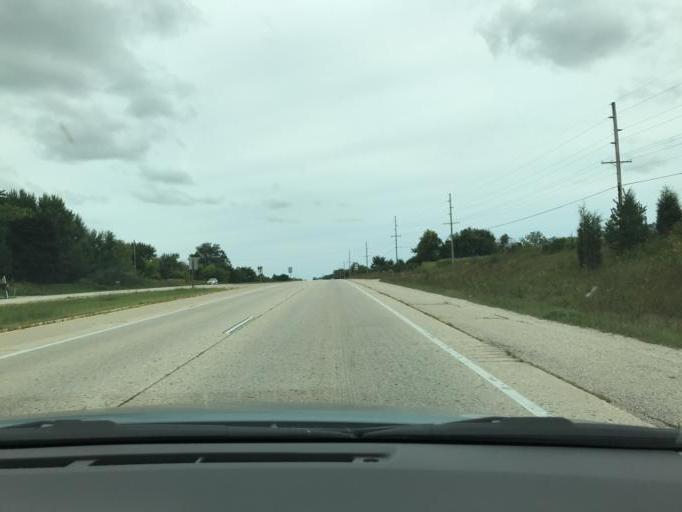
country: US
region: Wisconsin
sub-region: Kenosha County
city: Bristol
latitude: 42.5675
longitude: -88.0086
